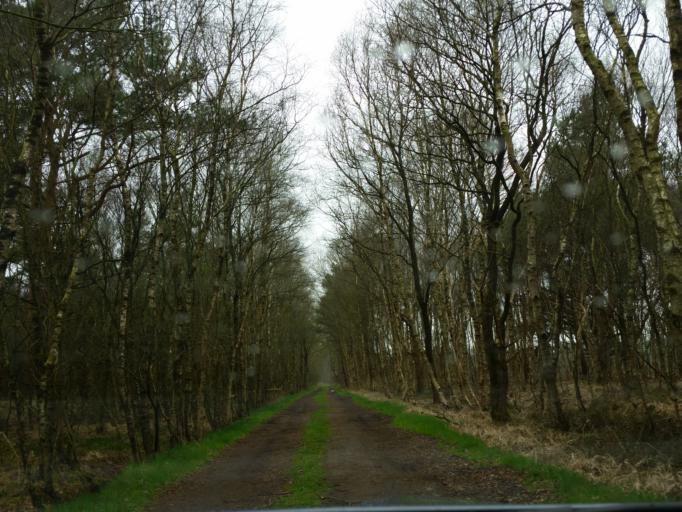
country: DE
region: Lower Saxony
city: Mittelstenahe
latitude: 53.6016
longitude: 8.9932
